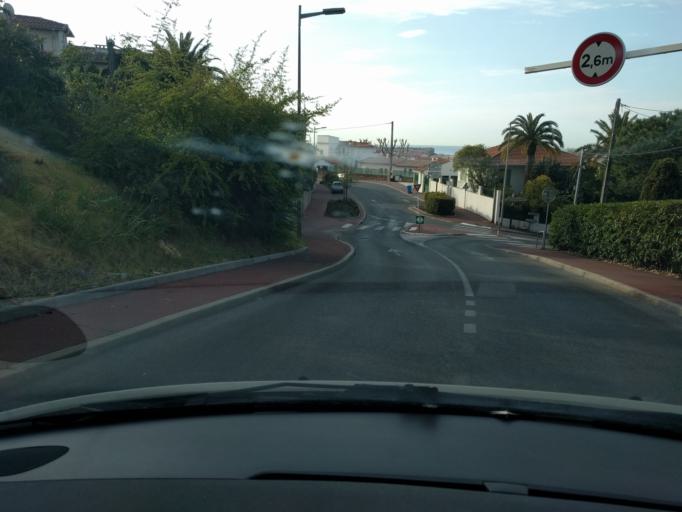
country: FR
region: Provence-Alpes-Cote d'Azur
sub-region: Departement des Alpes-Maritimes
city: Mandelieu-la-Napoule
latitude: 43.5597
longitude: 6.9728
